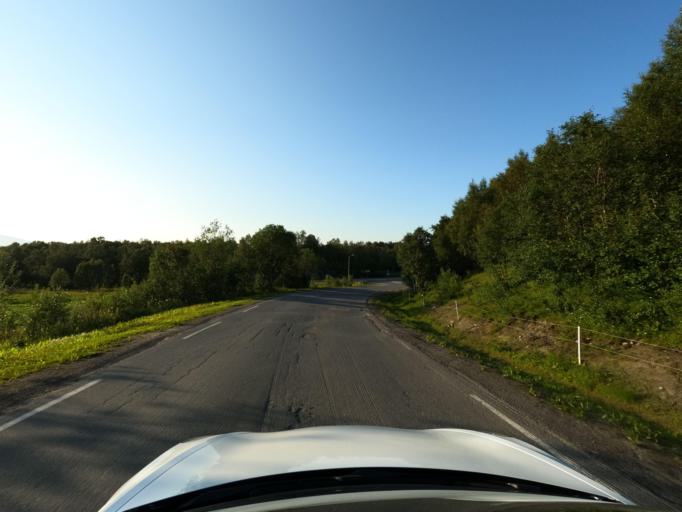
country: NO
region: Troms
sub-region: Skanland
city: Evenskjer
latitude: 68.4908
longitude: 16.7158
